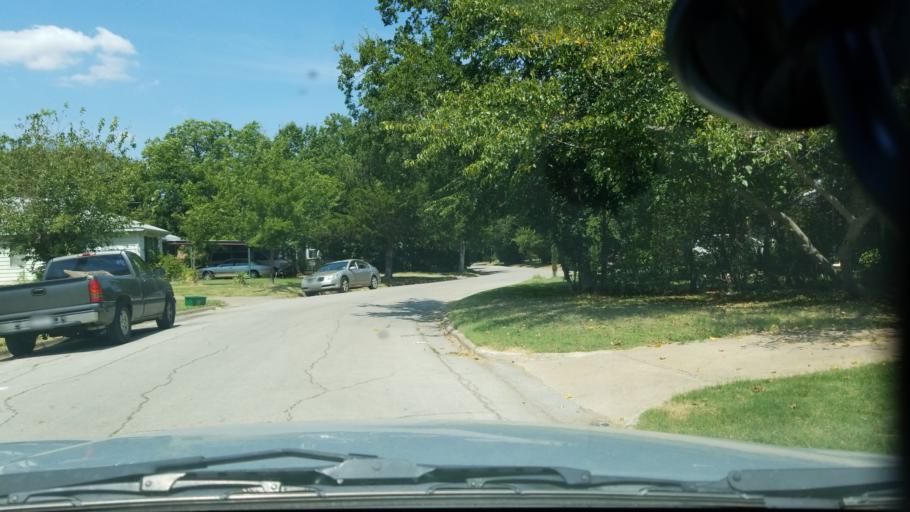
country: US
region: Texas
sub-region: Dallas County
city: Grand Prairie
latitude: 32.7512
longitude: -96.9527
